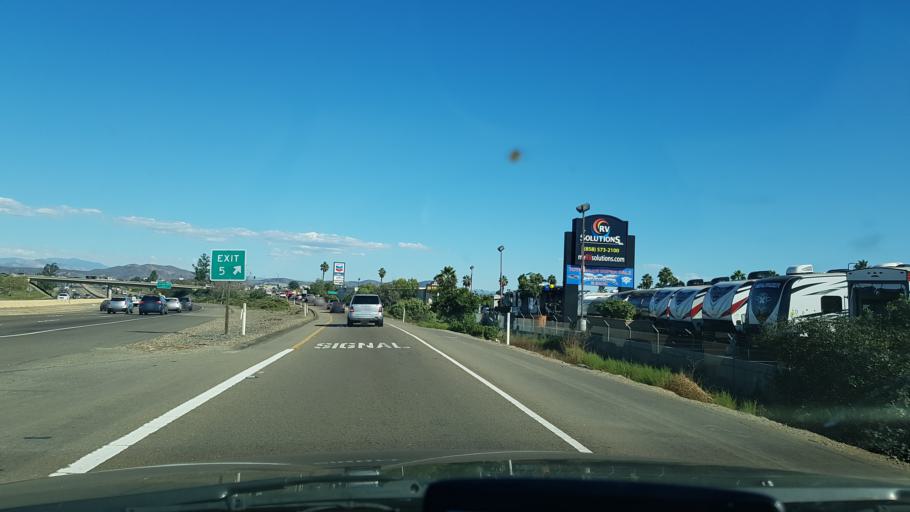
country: US
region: California
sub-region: San Diego County
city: La Jolla
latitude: 32.8371
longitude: -117.1556
